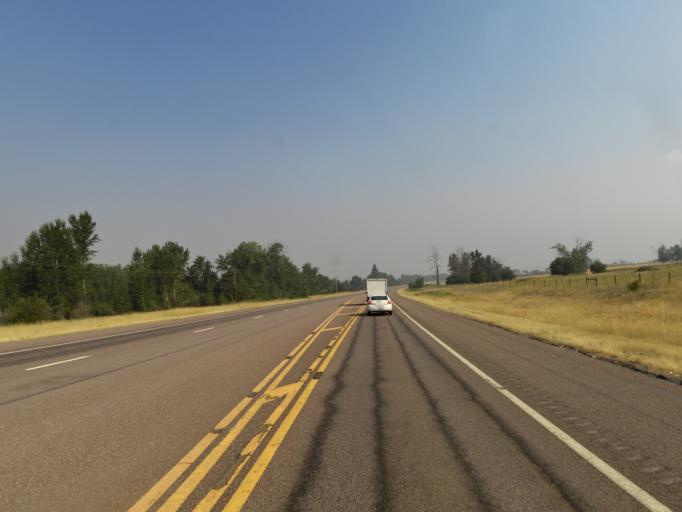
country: US
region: Montana
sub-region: Missoula County
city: Frenchtown
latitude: 47.1114
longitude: -114.0471
